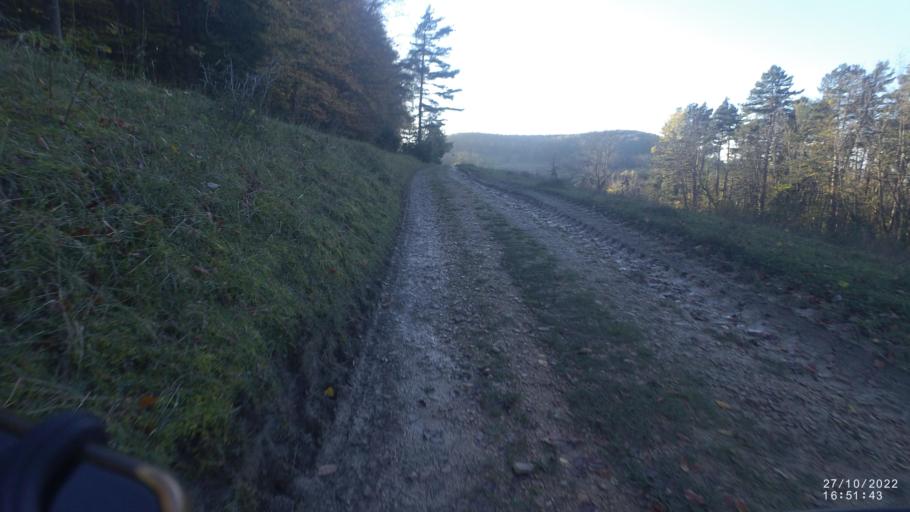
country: DE
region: Baden-Wuerttemberg
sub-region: Regierungsbezirk Stuttgart
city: Gingen an der Fils
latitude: 48.6450
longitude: 9.7559
